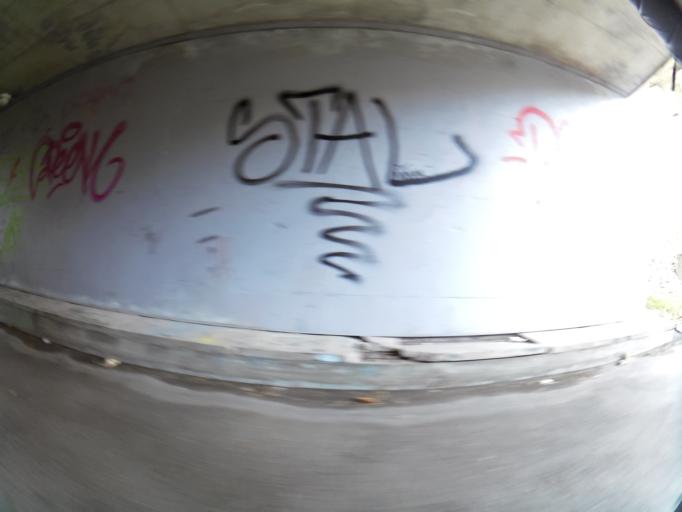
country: NO
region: Ostfold
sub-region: Sarpsborg
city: Sarpsborg
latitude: 59.2745
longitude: 11.0910
